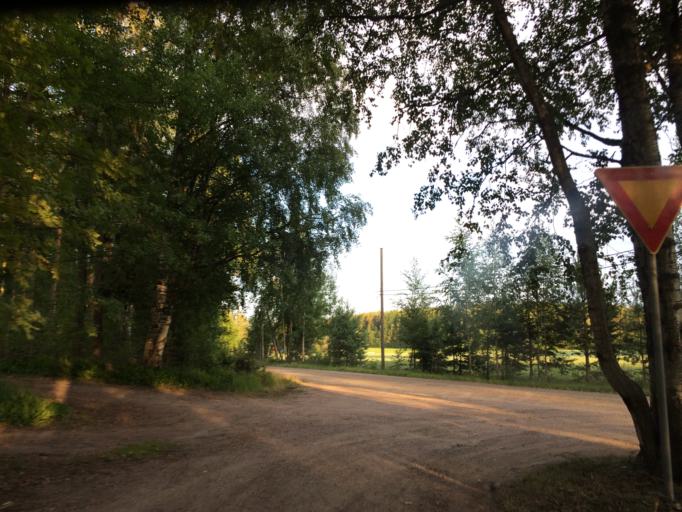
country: FI
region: Haeme
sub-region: Haemeenlinna
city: Janakkala
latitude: 60.8918
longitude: 24.6002
